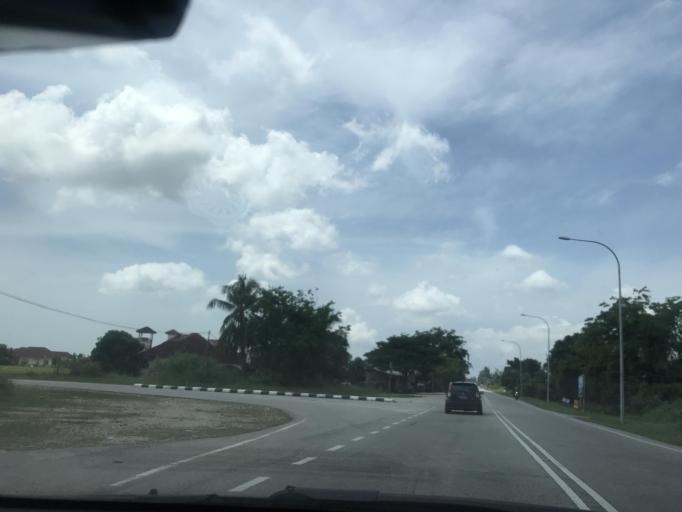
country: MY
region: Kelantan
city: Kota Bharu
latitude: 6.1495
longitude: 102.2131
